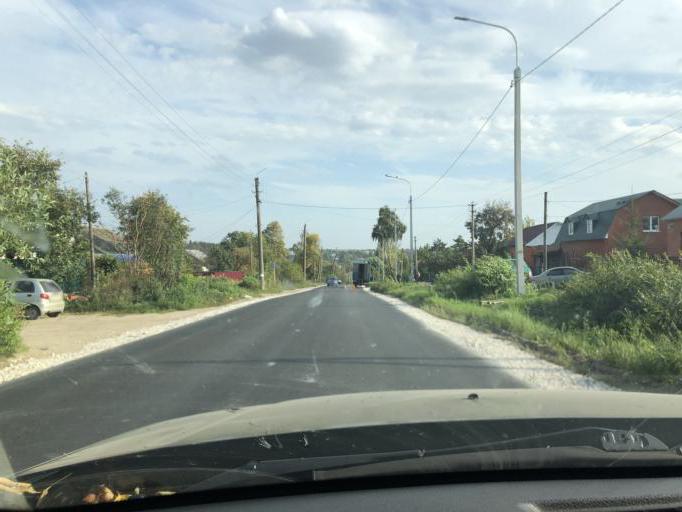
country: RU
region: Tula
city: Leninskiy
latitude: 54.2956
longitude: 37.4609
